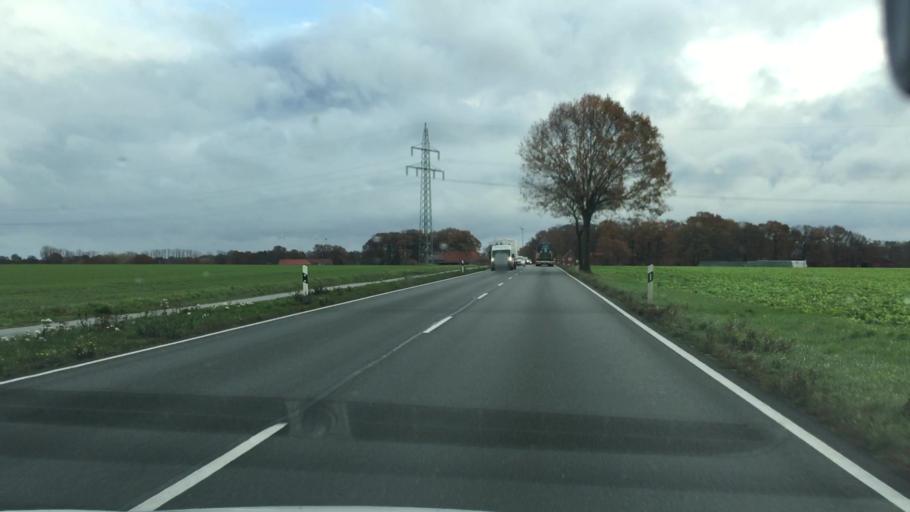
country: DE
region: Lower Saxony
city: Maasen
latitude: 52.6802
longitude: 8.8934
